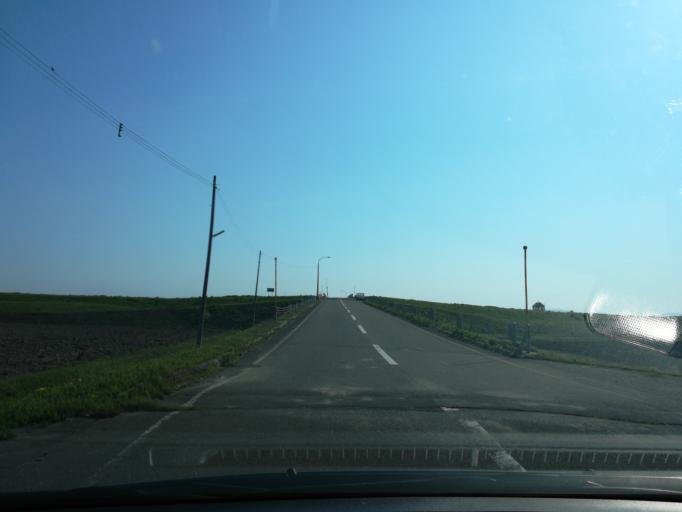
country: JP
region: Hokkaido
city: Iwamizawa
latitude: 43.1312
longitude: 141.6770
